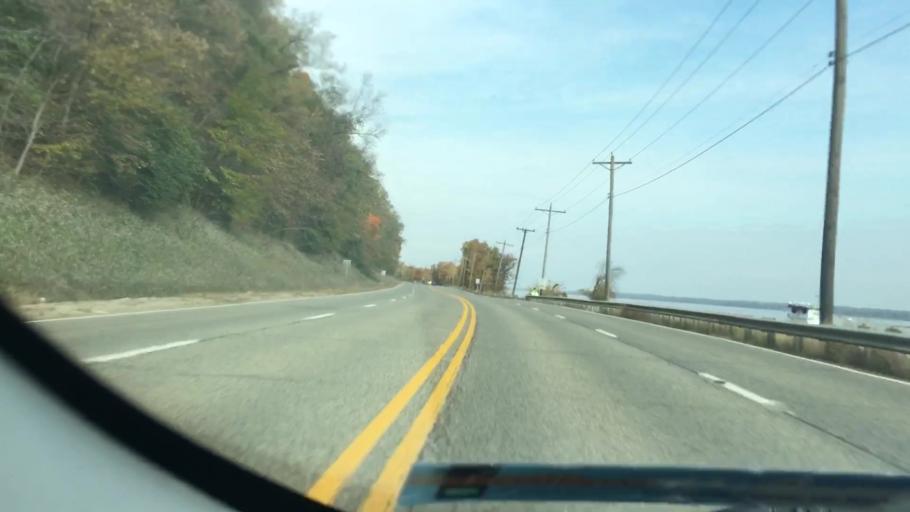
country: US
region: Illinois
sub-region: Peoria County
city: Peoria Heights
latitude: 40.7304
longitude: -89.5512
